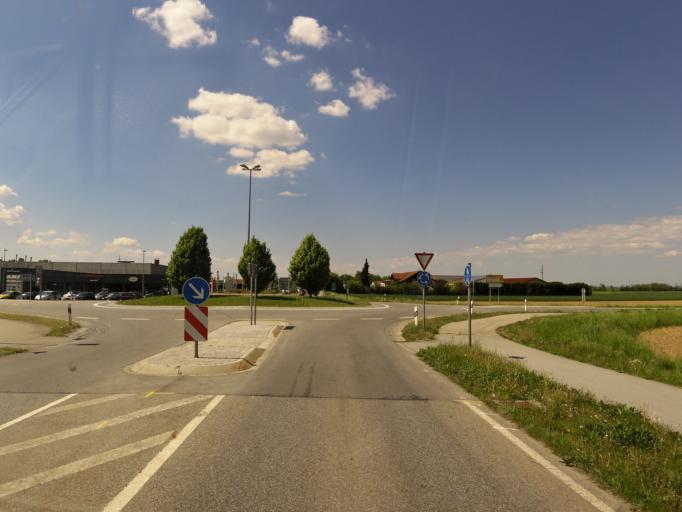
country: DE
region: Bavaria
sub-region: Lower Bavaria
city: Plattling
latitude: 48.7869
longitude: 12.8505
